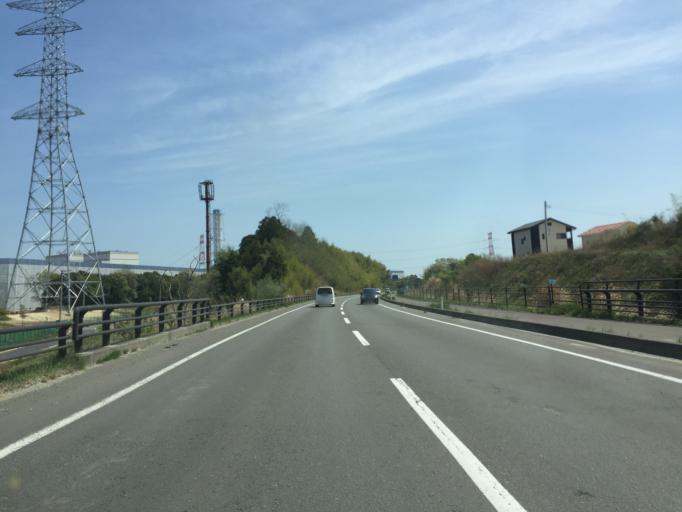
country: JP
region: Miyagi
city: Marumori
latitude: 37.8476
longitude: 140.9326
